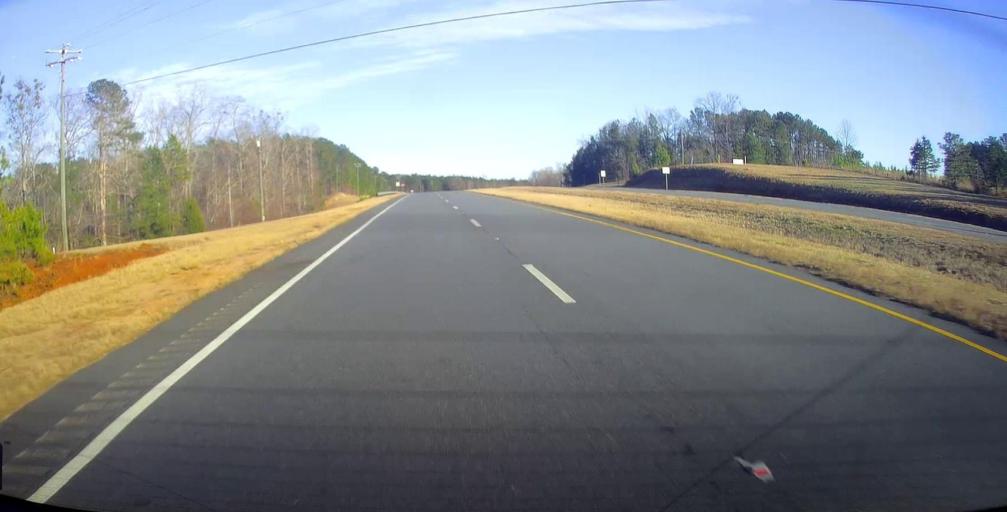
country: US
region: Georgia
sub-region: Upson County
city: Thomaston
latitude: 32.7913
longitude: -84.2538
